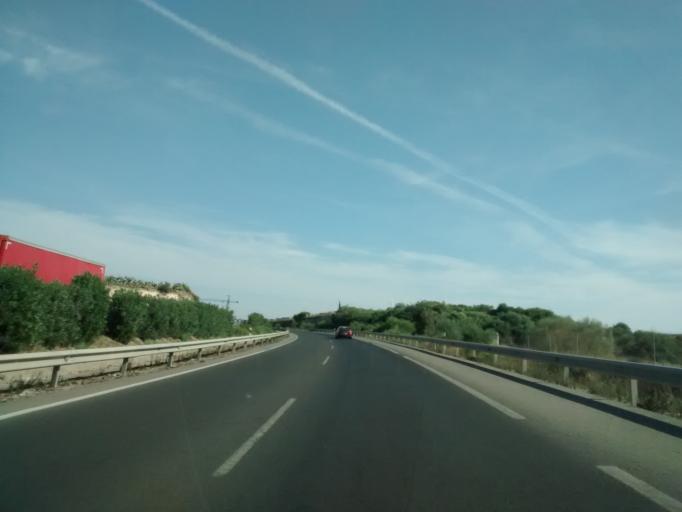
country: ES
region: Andalusia
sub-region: Provincia de Cadiz
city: Chiclana de la Frontera
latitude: 36.4241
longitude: -6.1141
